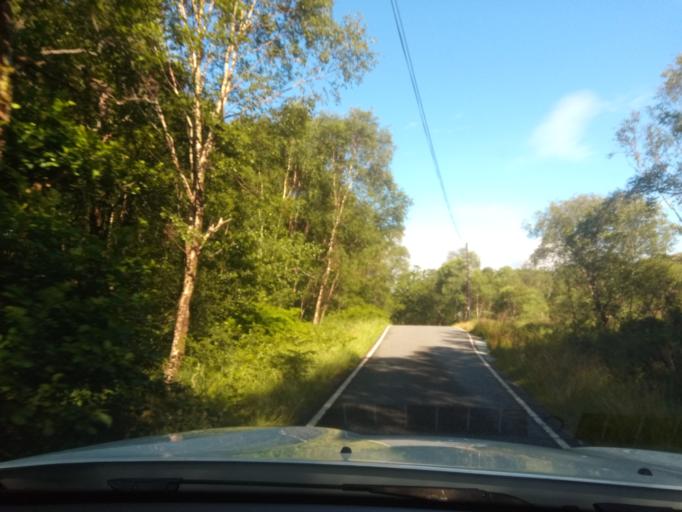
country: GB
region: Scotland
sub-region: Argyll and Bute
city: Isle Of Mull
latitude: 56.6869
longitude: -5.6588
